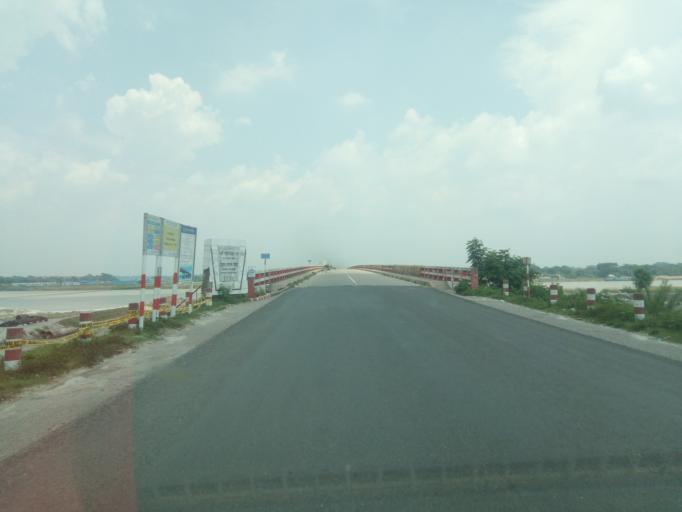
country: BD
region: Dhaka
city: Char Bhadrasan
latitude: 23.3783
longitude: 90.1138
